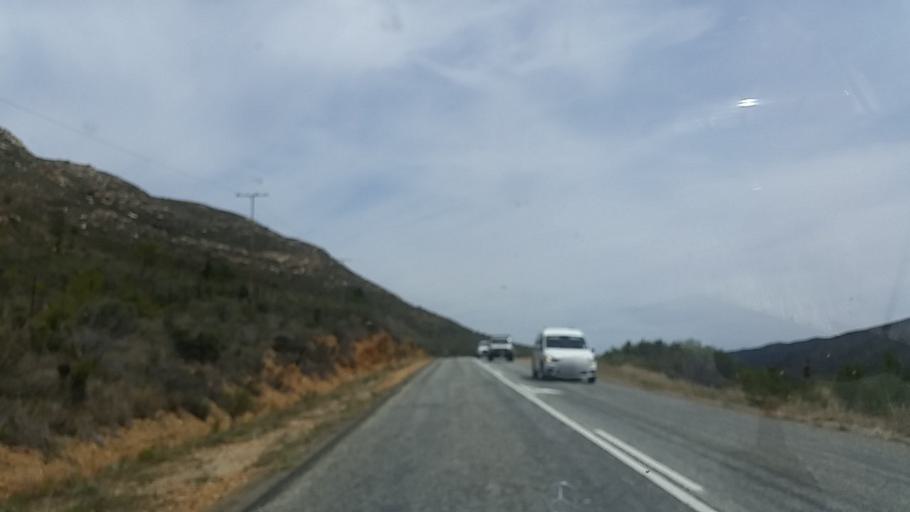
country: ZA
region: Western Cape
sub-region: Eden District Municipality
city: Knysna
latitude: -33.7458
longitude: 22.9876
